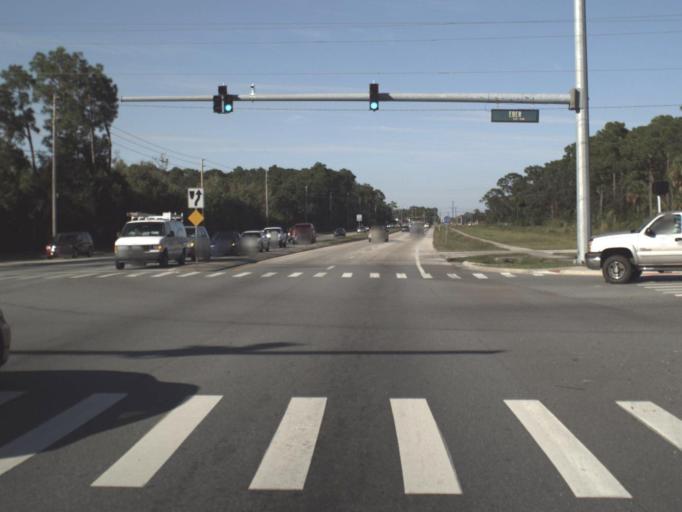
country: US
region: Florida
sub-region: Brevard County
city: June Park
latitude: 28.0513
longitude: -80.6712
